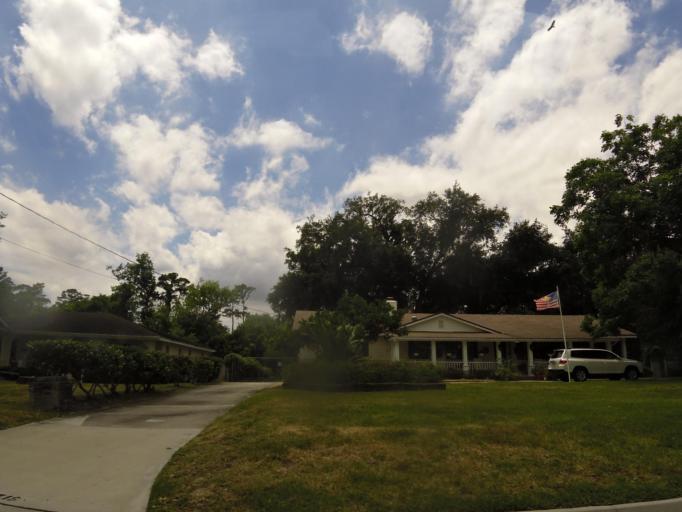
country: US
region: Florida
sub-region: Clay County
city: Orange Park
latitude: 30.1813
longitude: -81.6983
